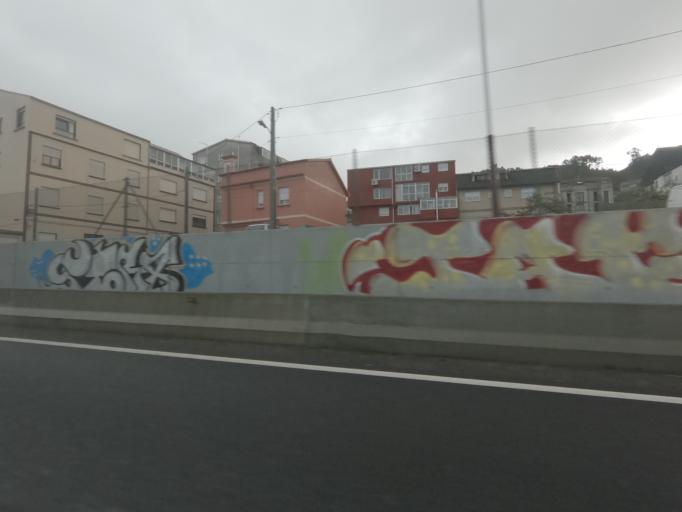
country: ES
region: Galicia
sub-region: Provincia de Pontevedra
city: Vigo
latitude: 42.2765
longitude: -8.6931
